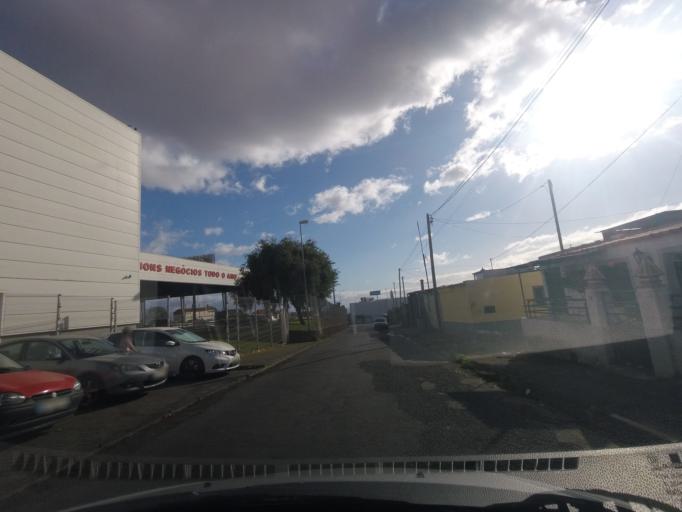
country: PT
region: Madeira
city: Camara de Lobos
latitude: 32.6554
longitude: -16.9425
